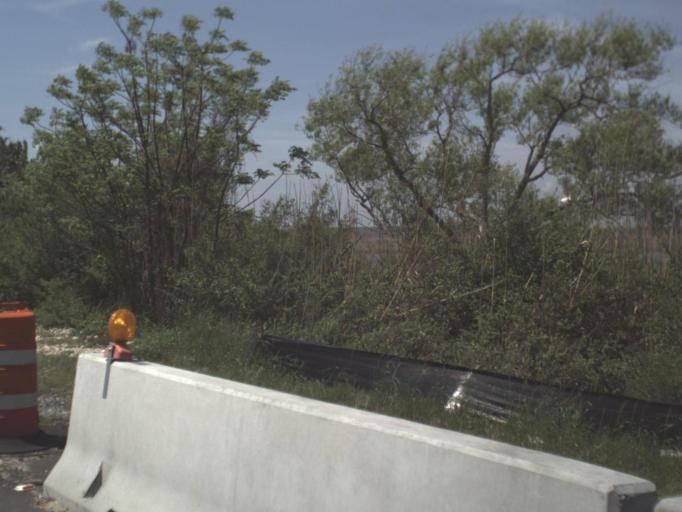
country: US
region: Florida
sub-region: Santa Rosa County
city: Pace
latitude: 30.5797
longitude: -87.1809
